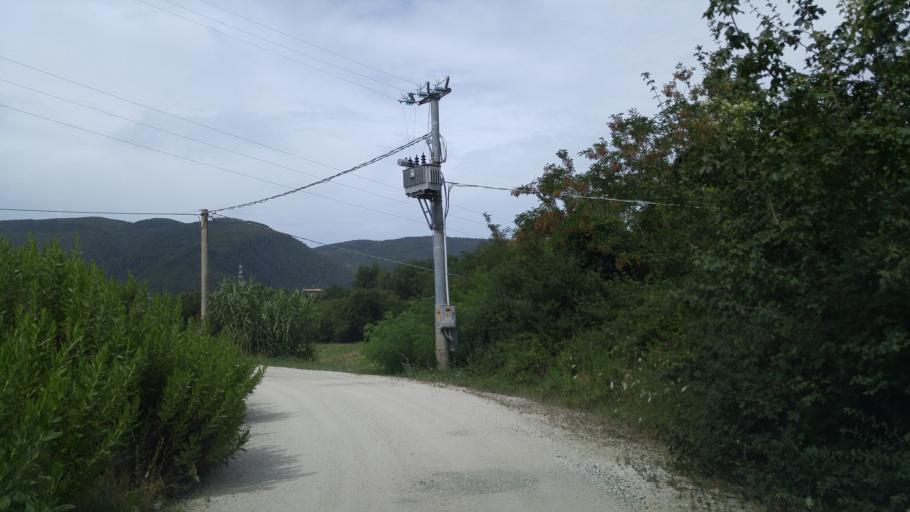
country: IT
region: The Marches
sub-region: Provincia di Pesaro e Urbino
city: Fossombrone
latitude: 43.6669
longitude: 12.7597
